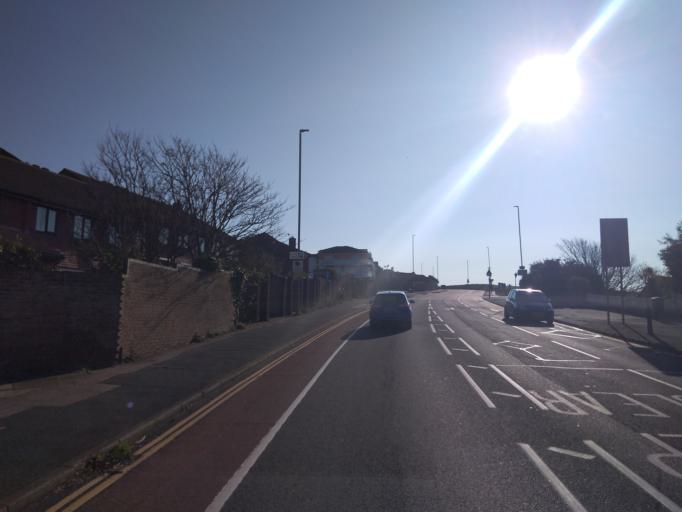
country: GB
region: England
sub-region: Brighton and Hove
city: Rottingdean
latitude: 50.8034
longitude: -0.0563
